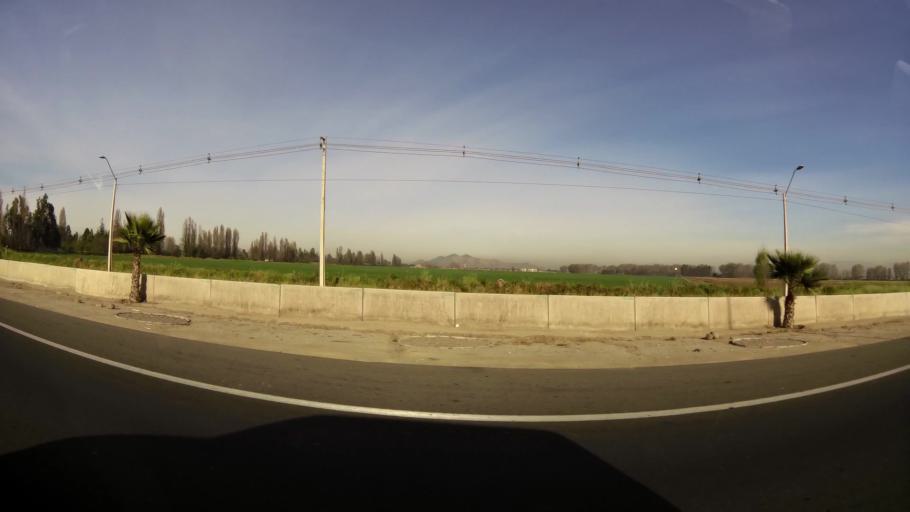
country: CL
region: Santiago Metropolitan
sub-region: Provincia de Santiago
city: La Pintana
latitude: -33.5782
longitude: -70.6116
